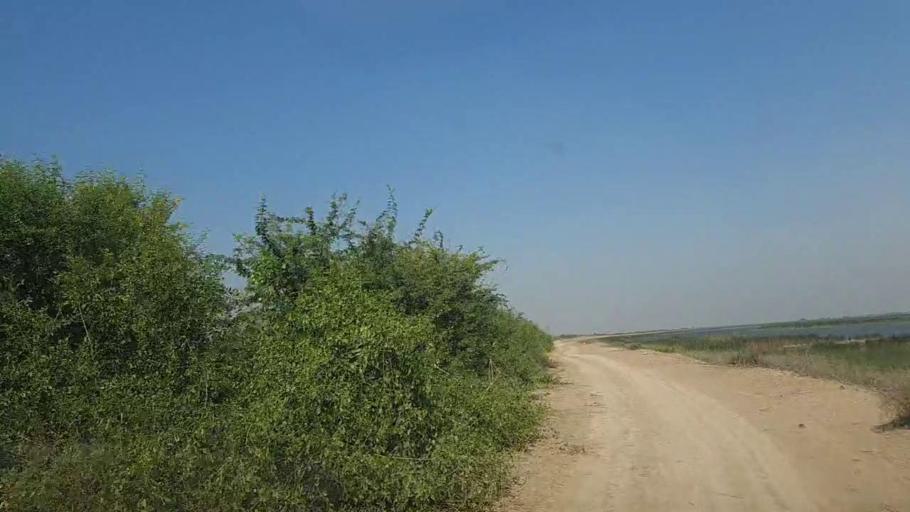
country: PK
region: Sindh
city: Daro Mehar
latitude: 24.9173
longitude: 68.0784
